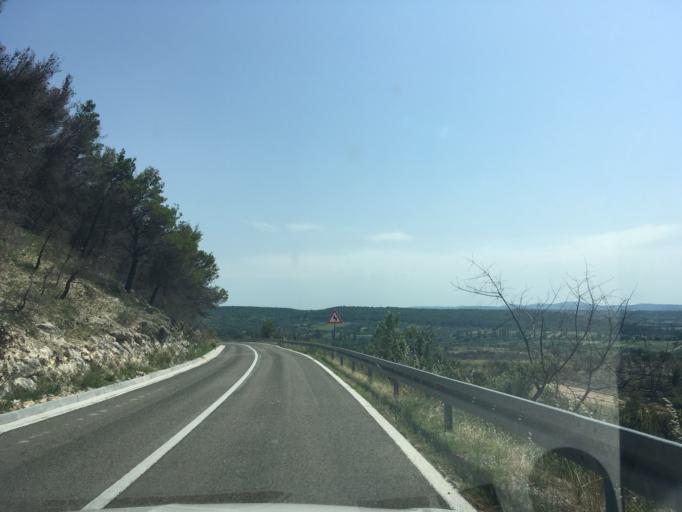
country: HR
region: Sibensko-Kniniska
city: Kistanje
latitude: 43.9415
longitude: 15.8322
